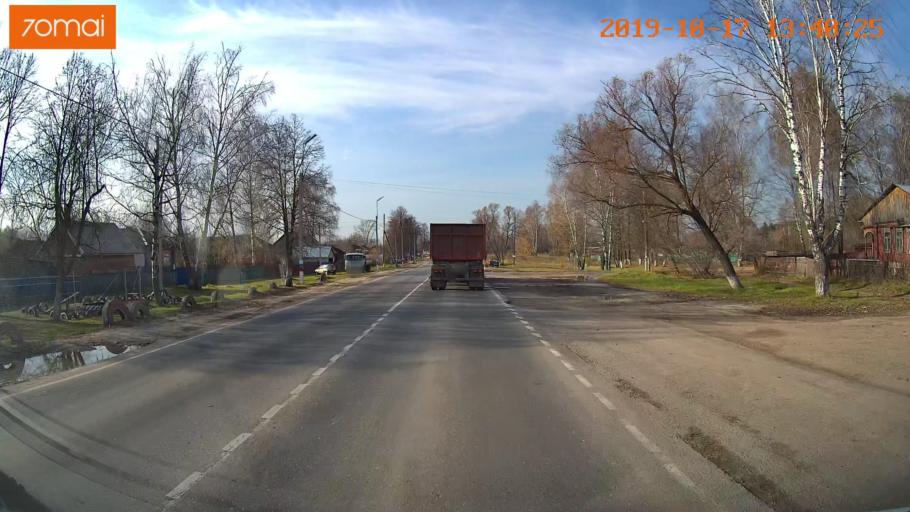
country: RU
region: Rjazan
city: Tuma
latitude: 55.1481
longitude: 40.5737
